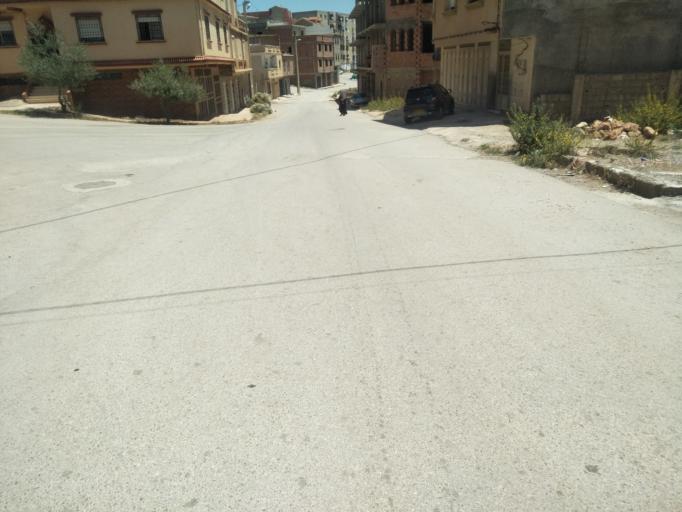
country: DZ
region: Tlemcen
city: Mansoura
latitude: 34.8742
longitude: -1.3690
